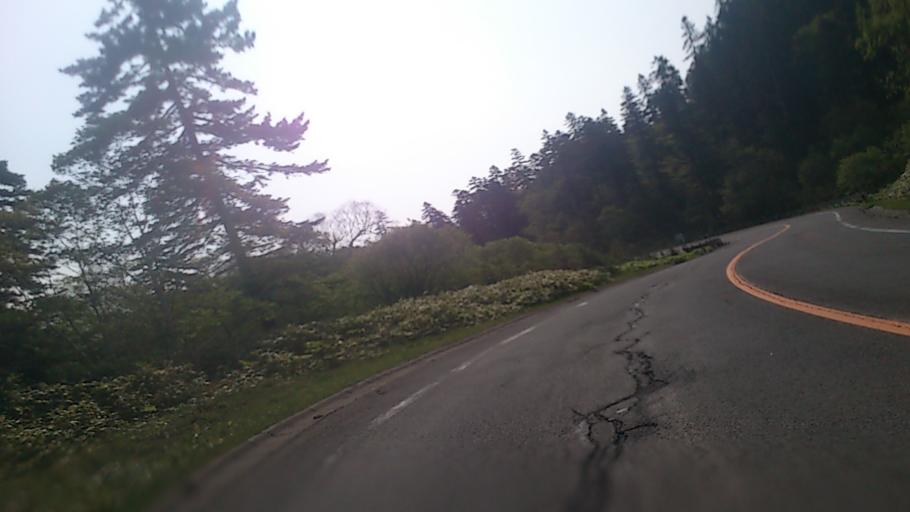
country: JP
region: Hokkaido
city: Bihoro
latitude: 43.4610
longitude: 144.2267
